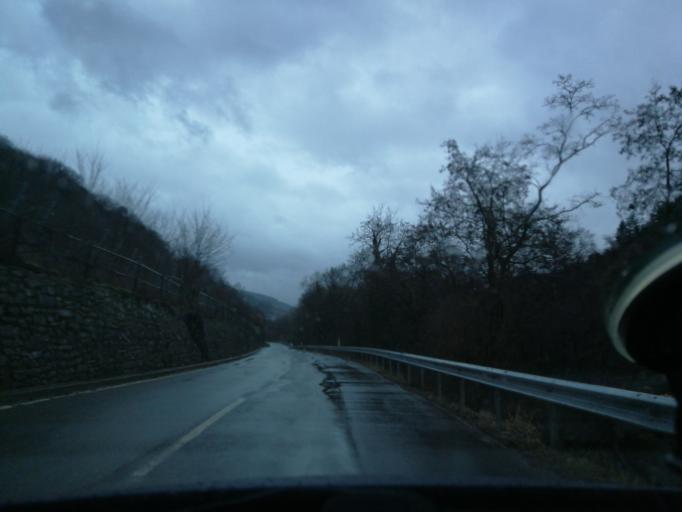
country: DE
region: Rheinland-Pfalz
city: Minheim
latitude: 49.8557
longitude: 6.9211
